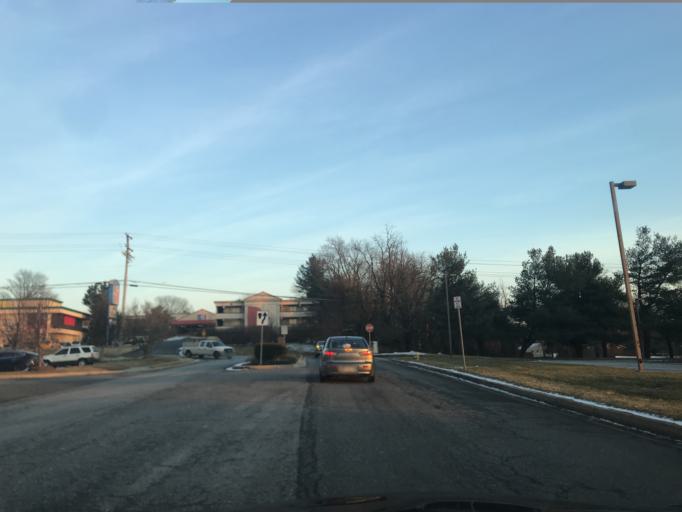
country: US
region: Maryland
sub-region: Harford County
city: Edgewood
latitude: 39.4522
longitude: -76.3090
